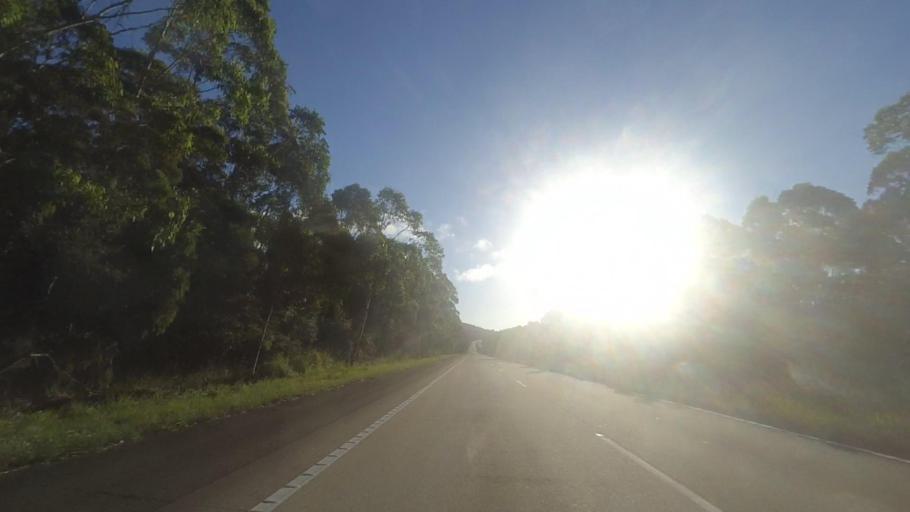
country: AU
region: New South Wales
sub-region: Great Lakes
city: Bulahdelah
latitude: -32.3795
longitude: 152.2706
